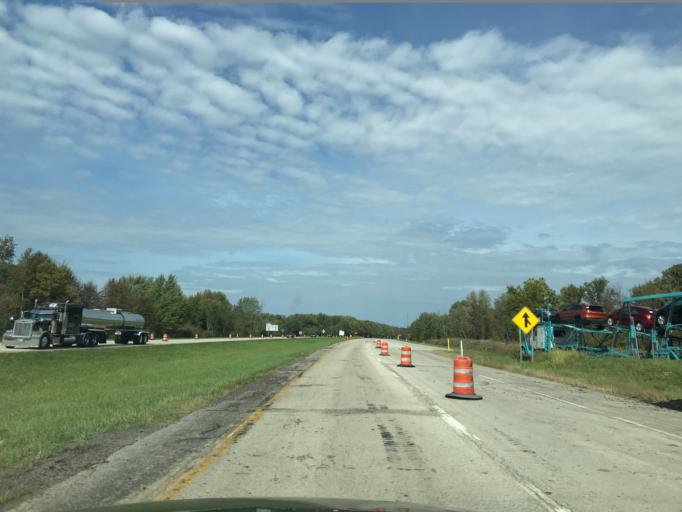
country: US
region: Ohio
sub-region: Ashtabula County
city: Ashtabula
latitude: 41.8095
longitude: -80.7587
